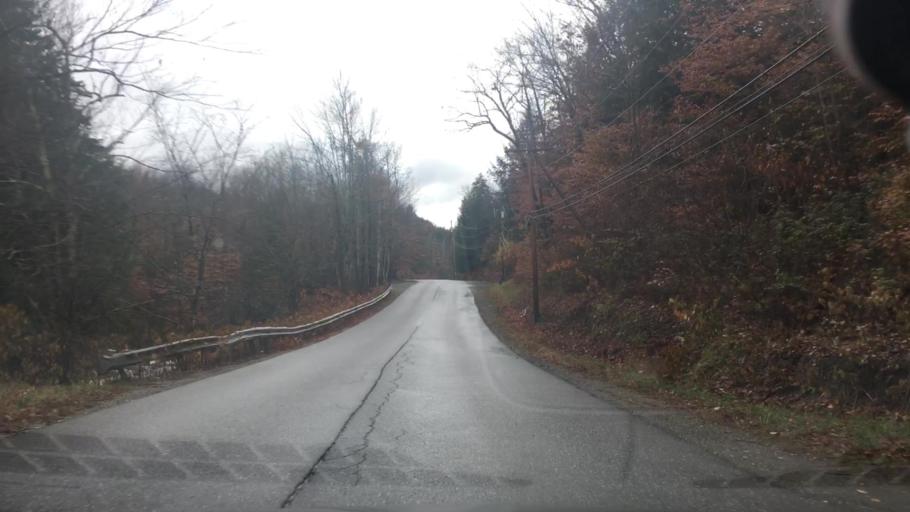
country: US
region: Vermont
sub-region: Lamoille County
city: Morristown
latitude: 44.5060
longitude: -72.7567
